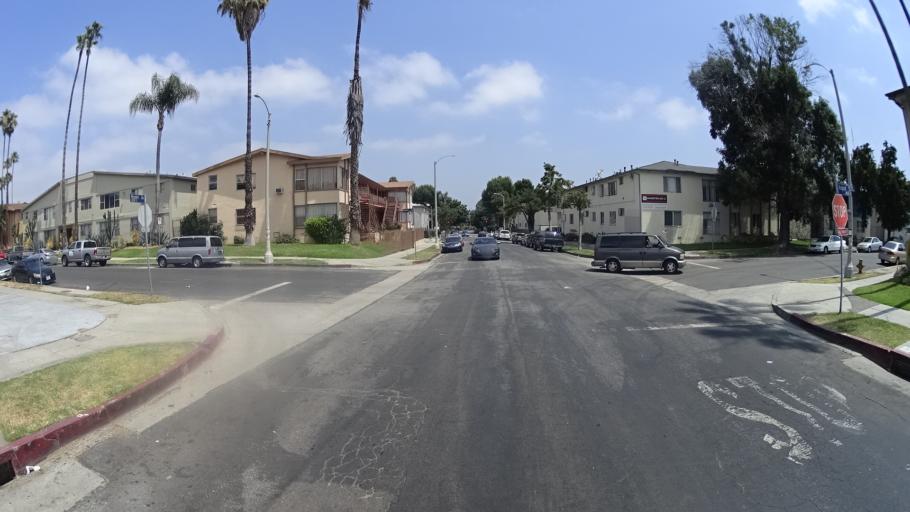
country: US
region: California
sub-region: Los Angeles County
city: View Park-Windsor Hills
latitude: 34.0171
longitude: -118.3505
